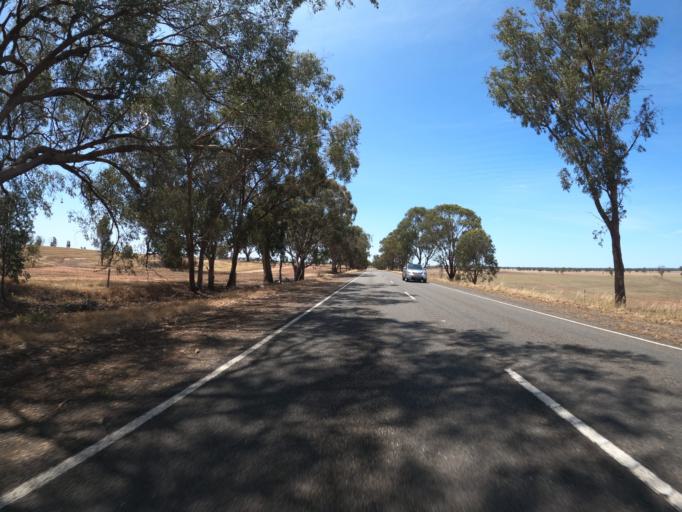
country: AU
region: Victoria
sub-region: Moira
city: Yarrawonga
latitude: -36.1028
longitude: 145.9915
